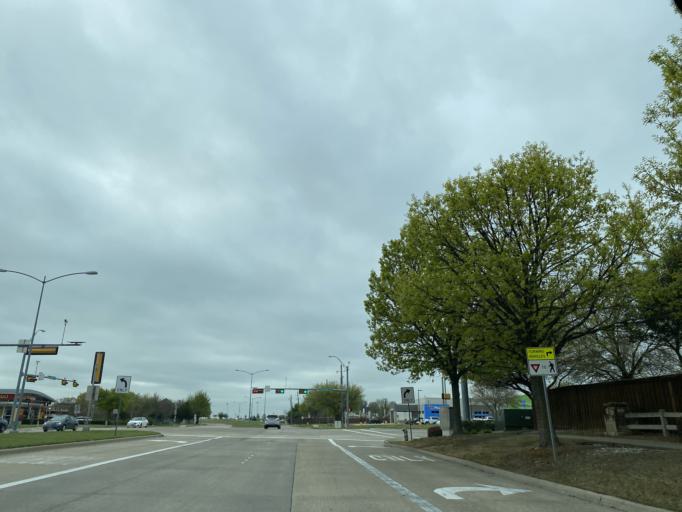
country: US
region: Texas
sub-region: Collin County
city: Fairview
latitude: 33.1157
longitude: -96.6289
